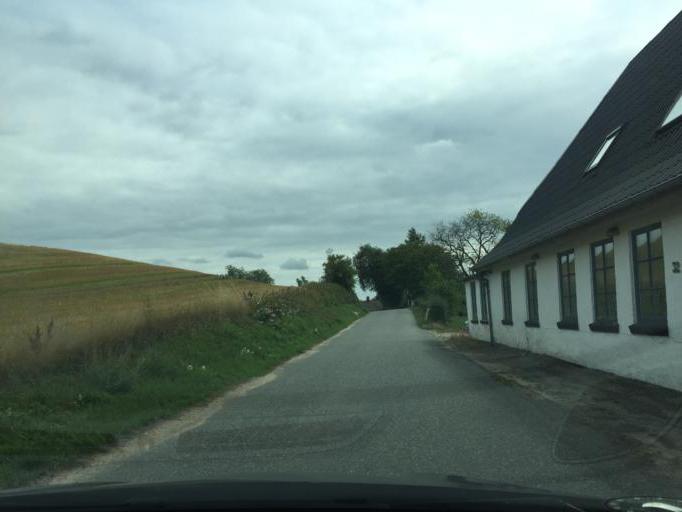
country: DK
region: South Denmark
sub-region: Assens Kommune
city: Vissenbjerg
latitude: 55.3516
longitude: 10.1214
